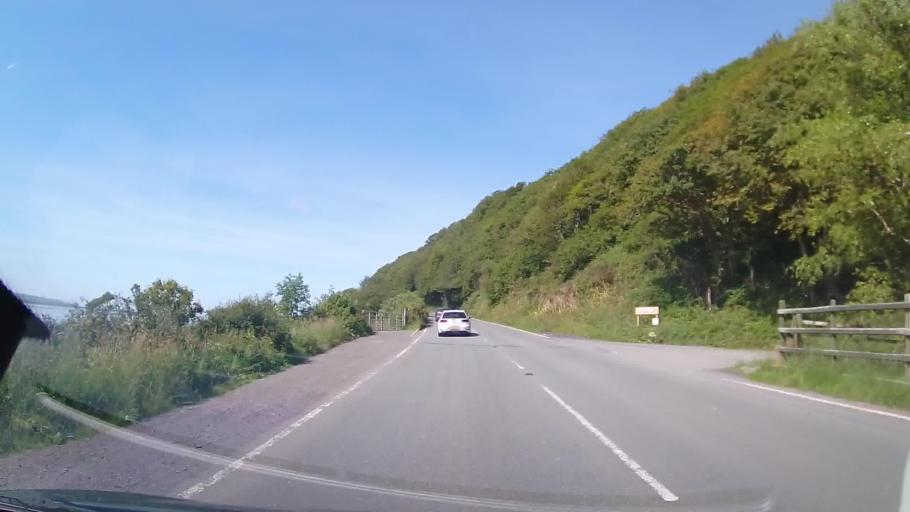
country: GB
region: Wales
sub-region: Gwynedd
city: Tywyn
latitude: 52.5559
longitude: -3.9777
